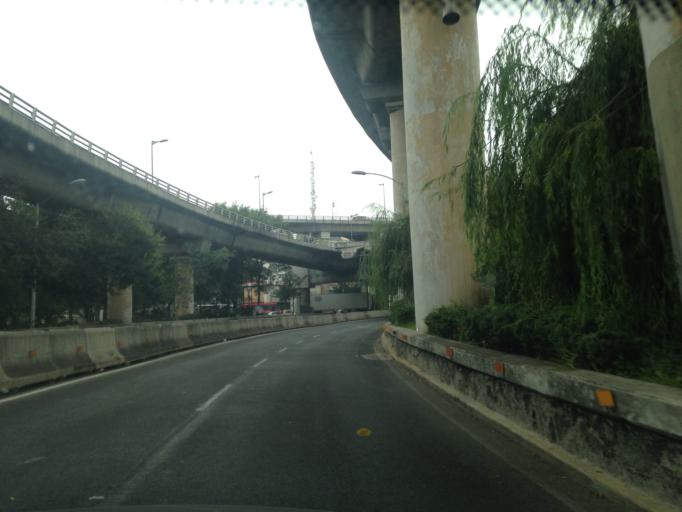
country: MX
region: Mexico City
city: Colonia del Valle
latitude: 19.3862
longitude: -99.1820
